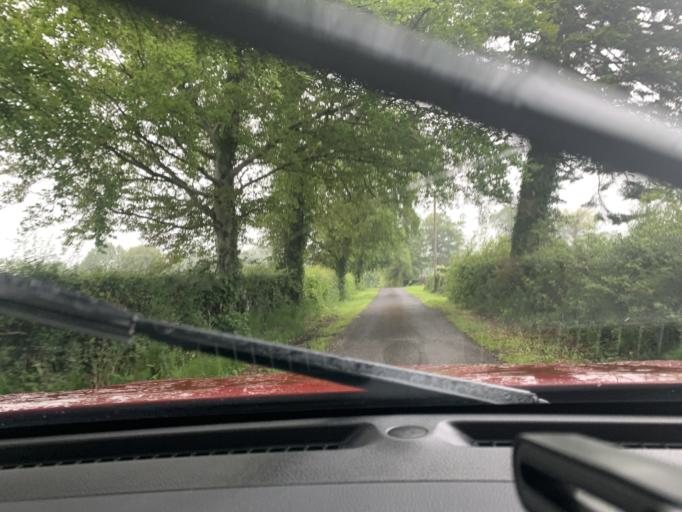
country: GB
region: Northern Ireland
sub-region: Fermanagh District
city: Enniskillen
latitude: 54.2623
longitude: -7.7382
